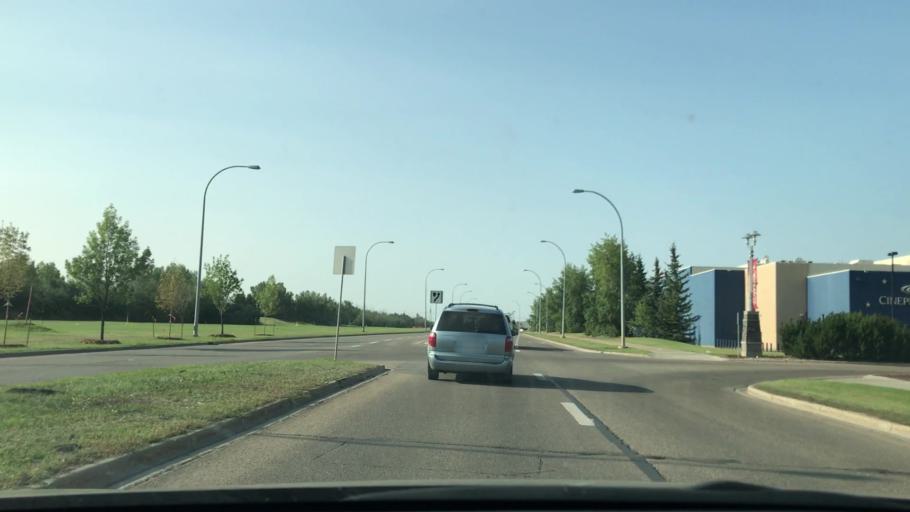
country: CA
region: Alberta
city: Edmonton
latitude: 53.4471
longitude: -113.4806
